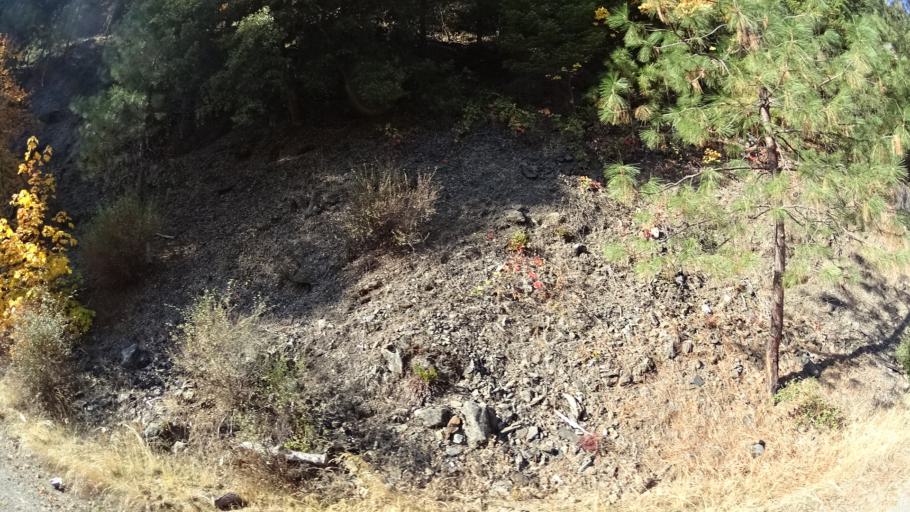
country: US
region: California
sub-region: Siskiyou County
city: Happy Camp
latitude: 41.7681
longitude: -123.0272
